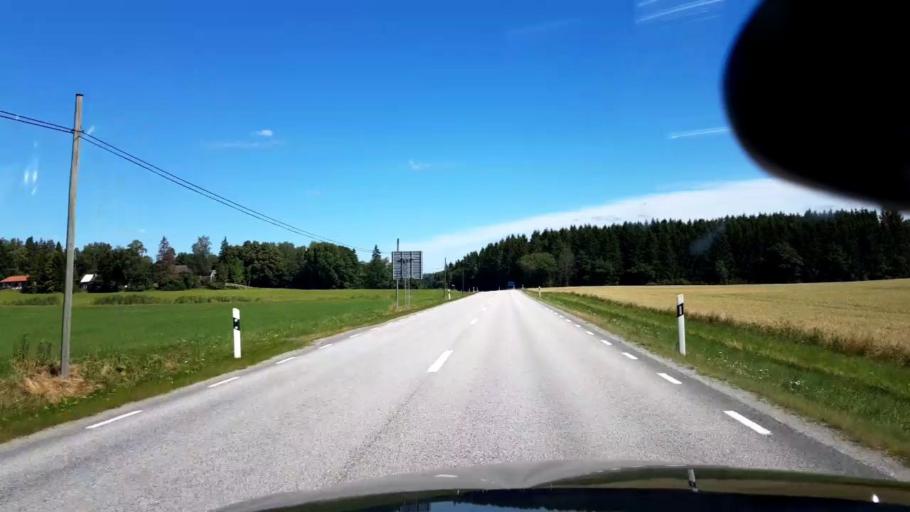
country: SE
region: Uppsala
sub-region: Habo Kommun
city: Balsta
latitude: 59.6326
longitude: 17.6017
